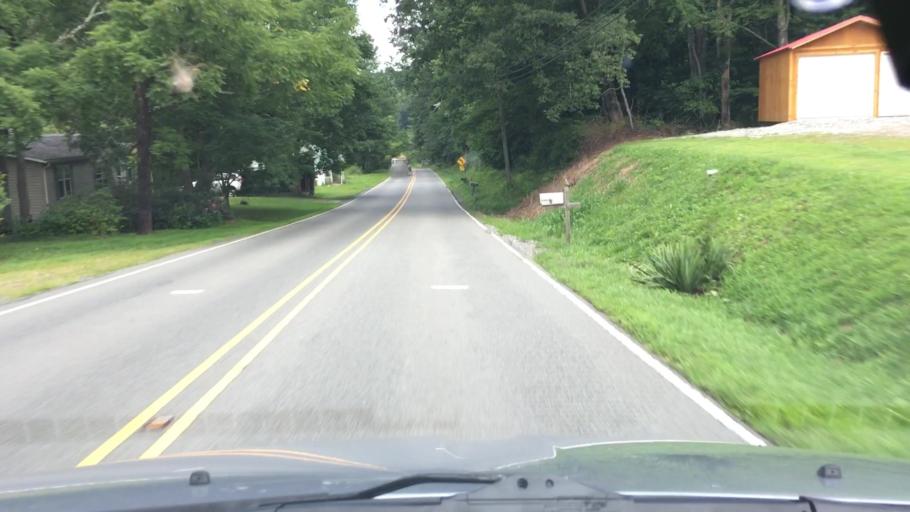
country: US
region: North Carolina
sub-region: Yancey County
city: Burnsville
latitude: 35.8412
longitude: -82.1900
